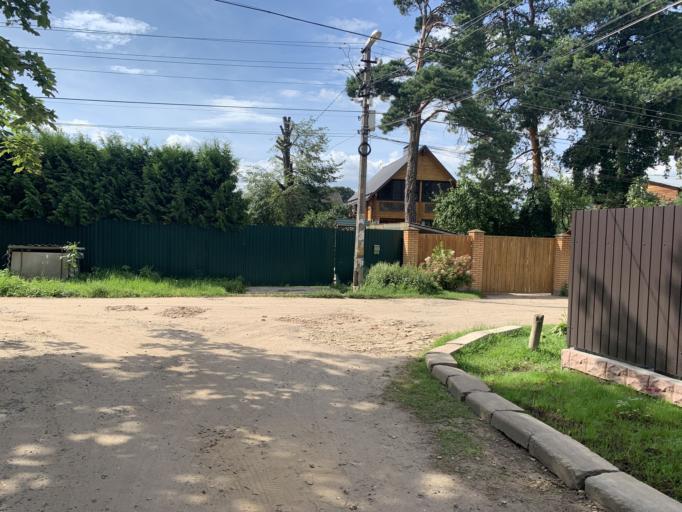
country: RU
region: Moskovskaya
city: Mamontovka
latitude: 55.9859
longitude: 37.8034
